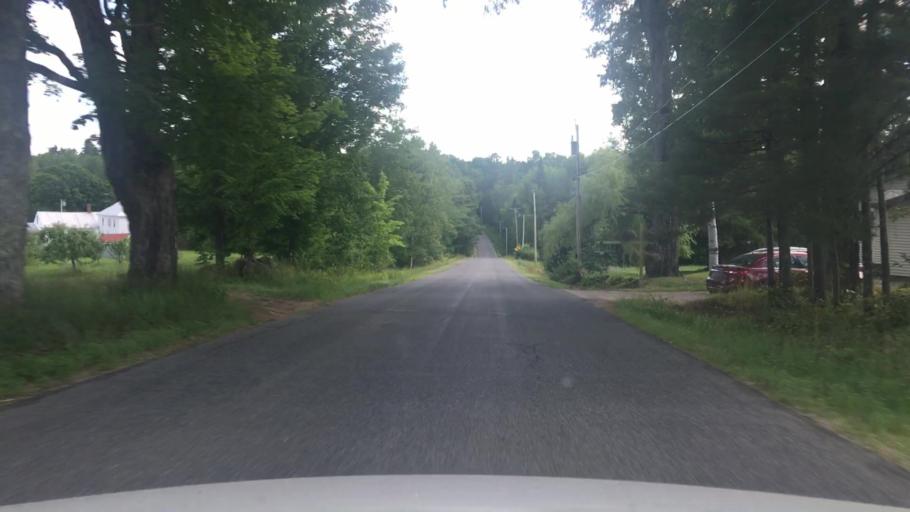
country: US
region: Maine
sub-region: Franklin County
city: Wilton
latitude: 44.6205
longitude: -70.2337
